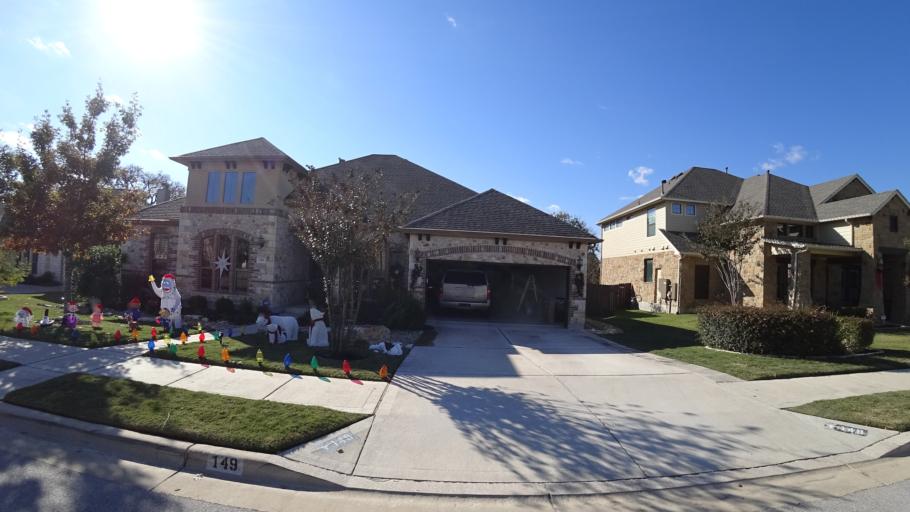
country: US
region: Texas
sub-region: Williamson County
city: Brushy Creek
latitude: 30.4875
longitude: -97.7277
